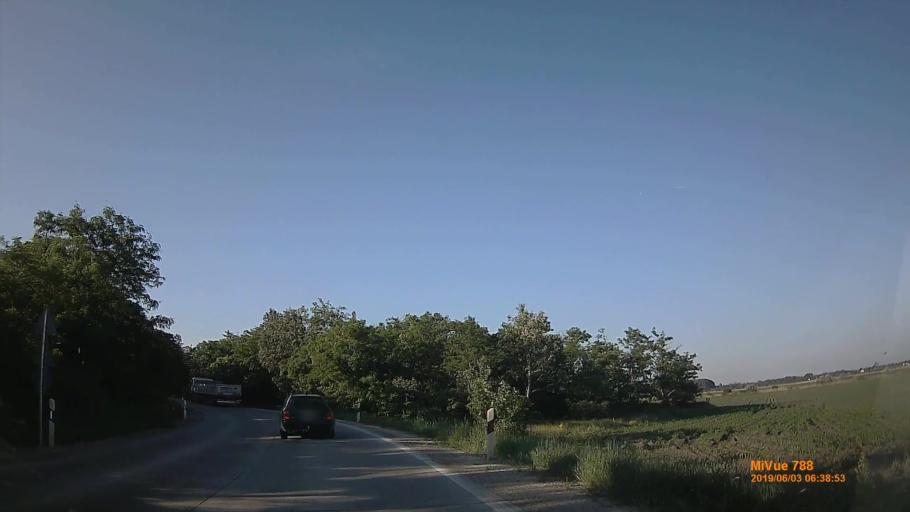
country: HU
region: Pest
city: Dunavarsany
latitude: 47.2917
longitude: 19.0957
